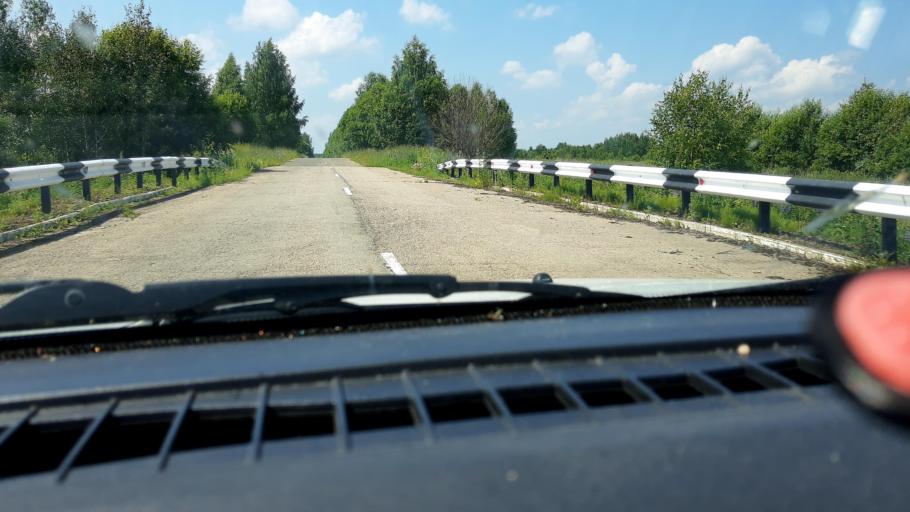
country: RU
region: Nizjnij Novgorod
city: Sharanga
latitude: 57.0586
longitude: 46.5984
